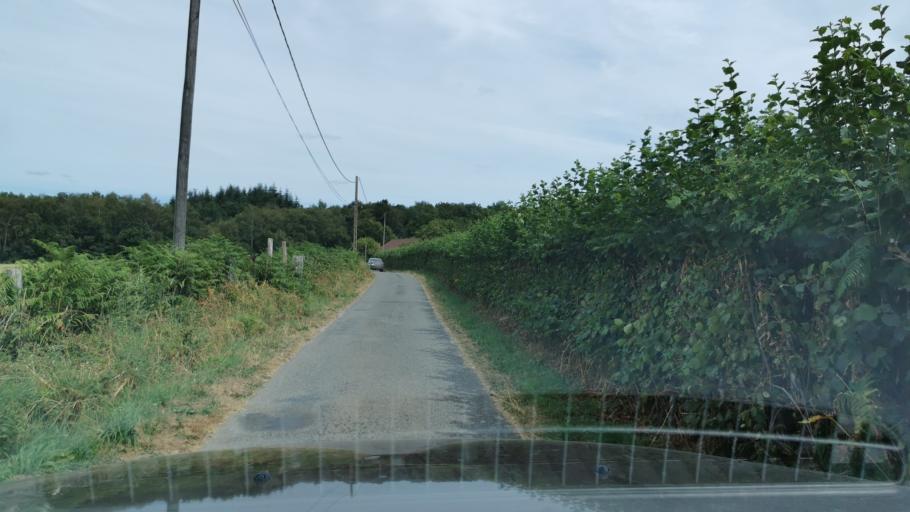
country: FR
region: Bourgogne
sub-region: Departement de Saone-et-Loire
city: Saint-Berain-sous-Sanvignes
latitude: 46.8014
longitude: 4.2654
